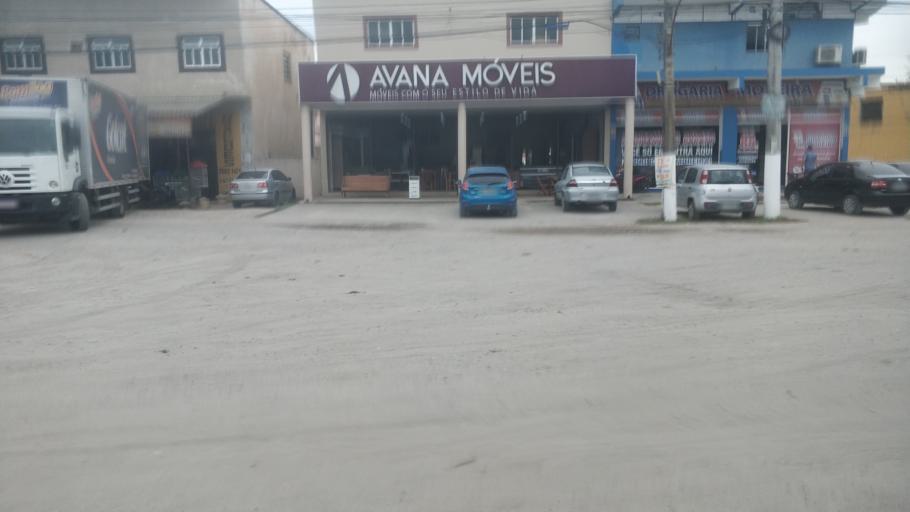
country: BR
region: Rio de Janeiro
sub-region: Seropedica
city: Seropedica
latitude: -22.7957
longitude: -43.6477
